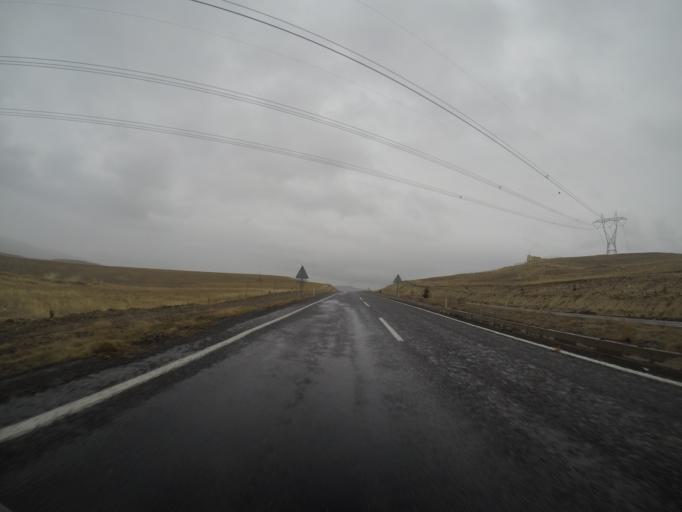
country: TR
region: Nevsehir
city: Avanos
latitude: 38.7080
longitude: 34.8793
